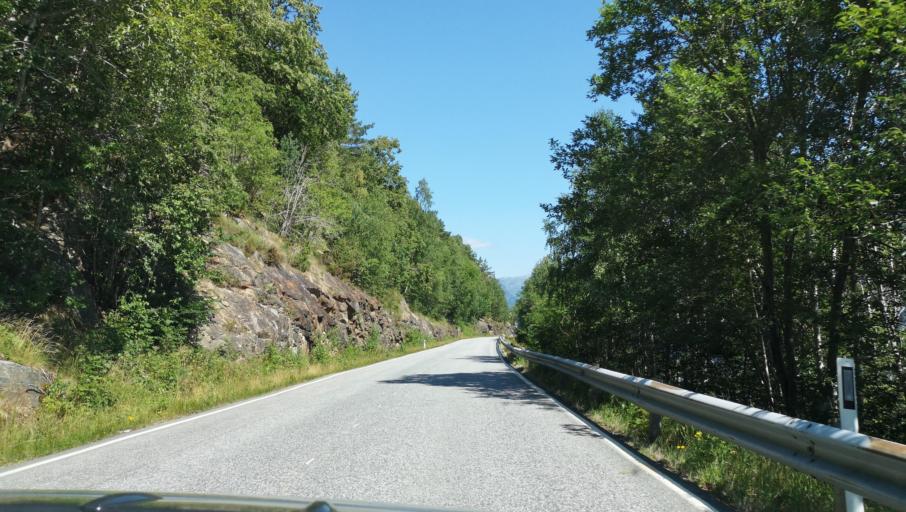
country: NO
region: Hordaland
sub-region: Ulvik
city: Ulvik
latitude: 60.5014
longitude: 6.8995
